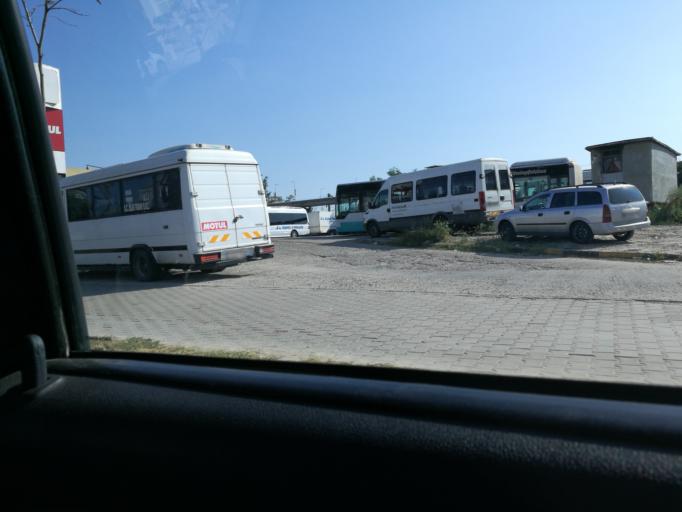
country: RO
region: Iasi
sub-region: Municipiul Iasi
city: Iasi
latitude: 47.1719
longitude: 27.5591
